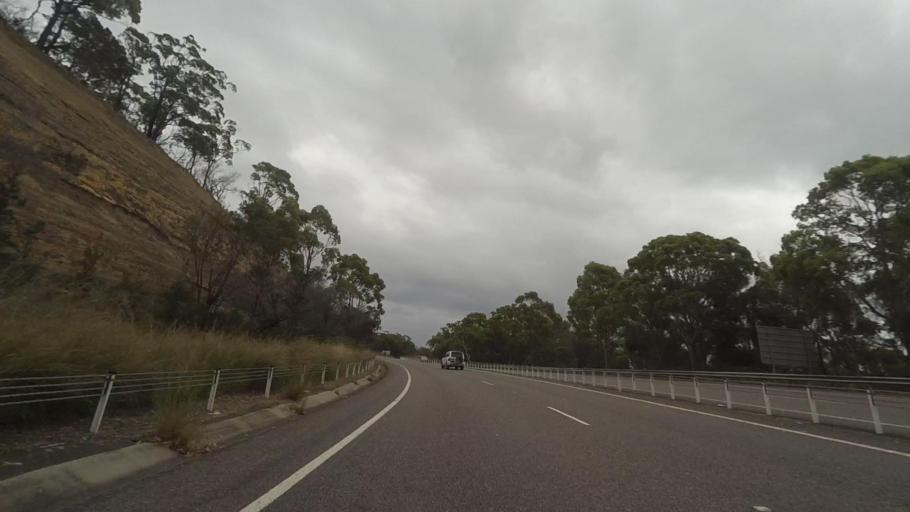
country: AU
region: New South Wales
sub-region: Wyong Shire
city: Kingfisher Shores
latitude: -33.1304
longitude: 151.6236
